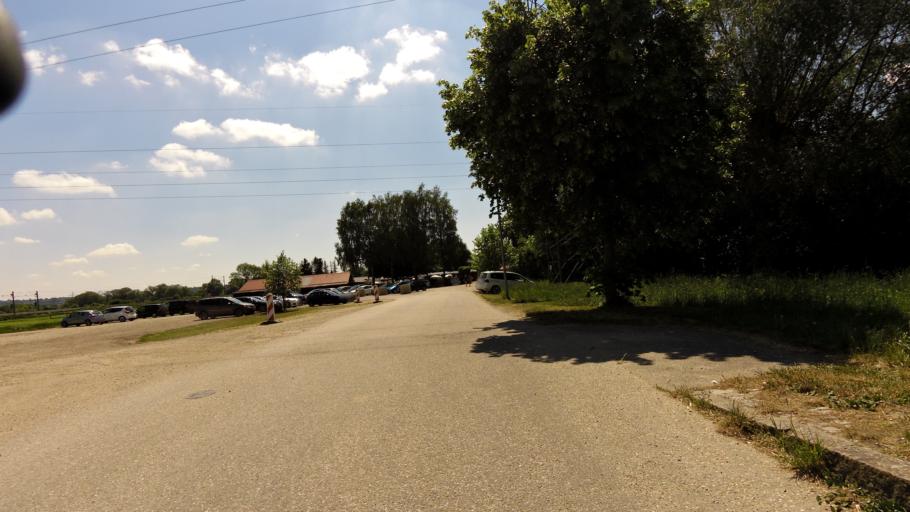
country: DE
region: Bavaria
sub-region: Lower Bavaria
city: Tiefenbach
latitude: 48.5461
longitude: 12.1007
